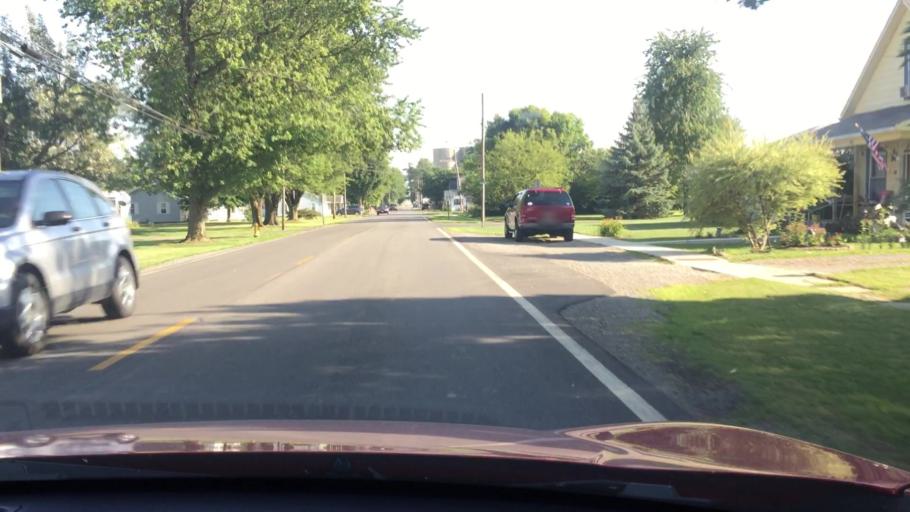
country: US
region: Ohio
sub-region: Hardin County
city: Ada
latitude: 40.7096
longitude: -83.8422
